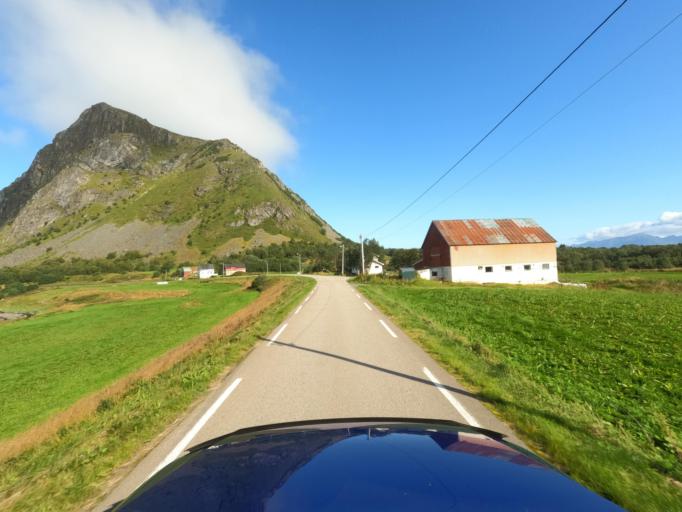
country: NO
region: Nordland
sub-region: Vestvagoy
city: Evjen
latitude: 68.3224
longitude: 14.1076
